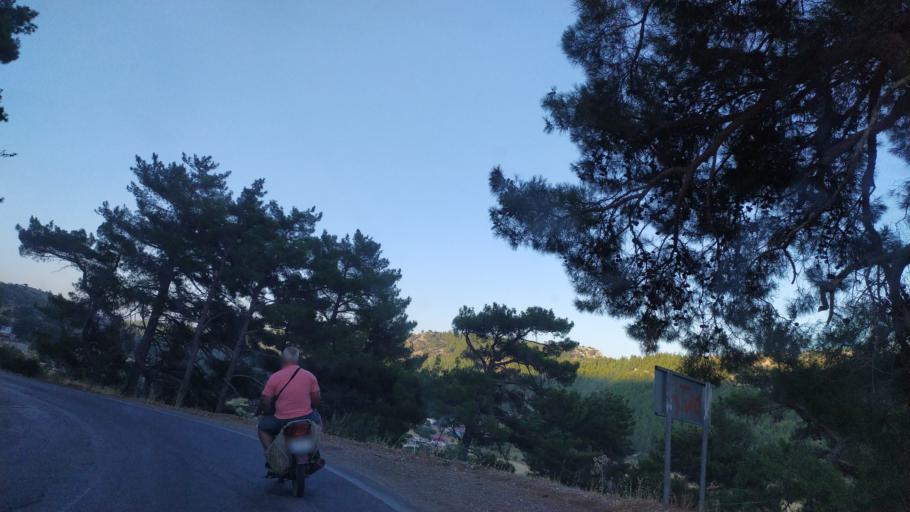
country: TR
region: Mersin
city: Akdere
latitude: 36.3379
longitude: 33.7528
